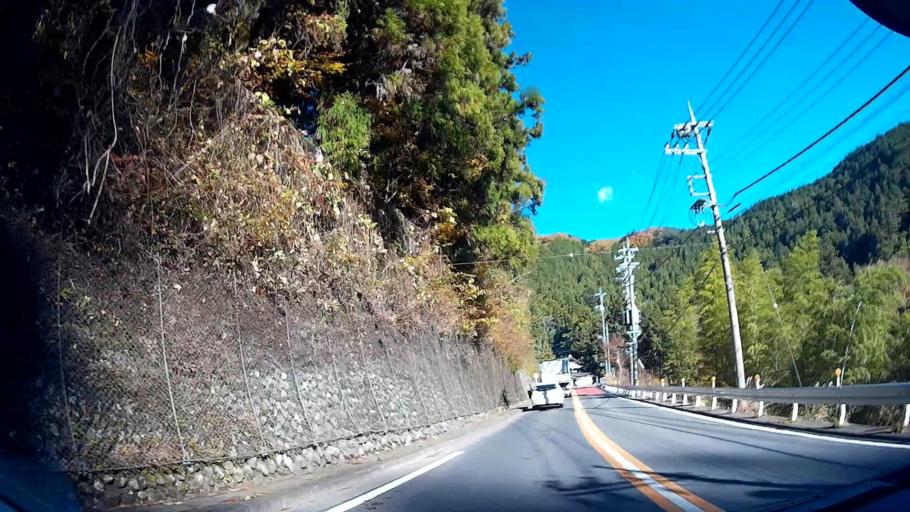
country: JP
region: Tokyo
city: Itsukaichi
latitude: 35.7244
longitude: 139.1584
